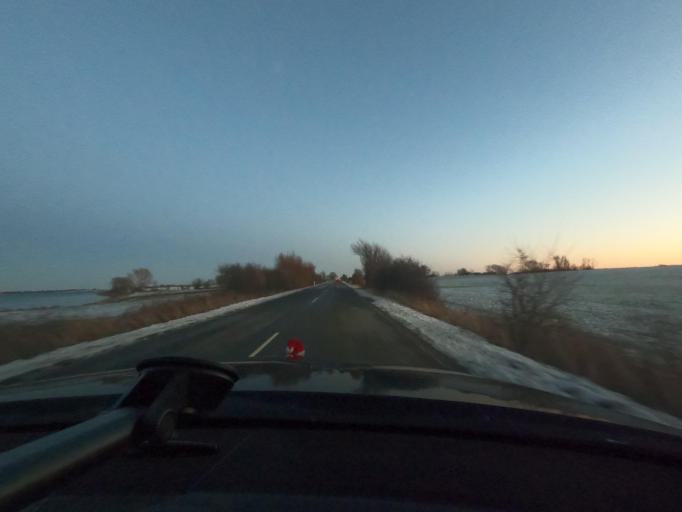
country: DK
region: South Denmark
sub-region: Sonderborg Kommune
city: Horuphav
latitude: 54.8675
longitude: 9.9546
